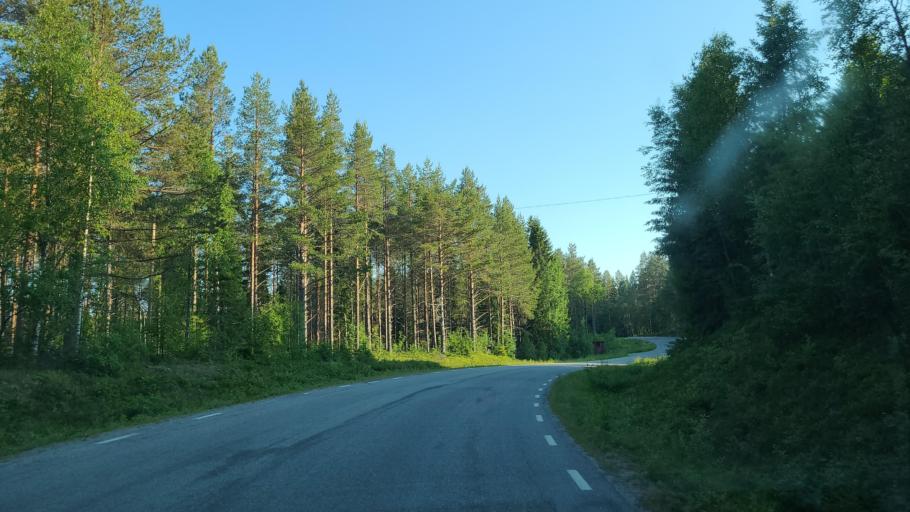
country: SE
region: Vaesterbotten
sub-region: Skelleftea Kommun
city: Burea
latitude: 64.3550
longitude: 21.3380
